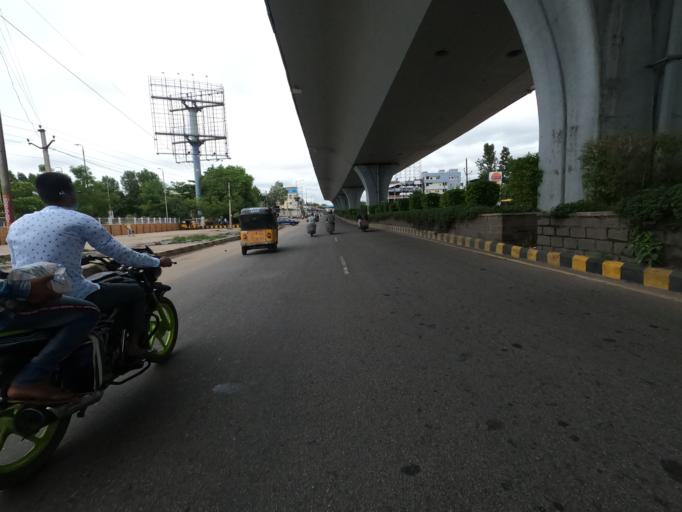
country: IN
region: Telangana
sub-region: Hyderabad
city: Hyderabad
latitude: 17.3352
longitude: 78.4267
